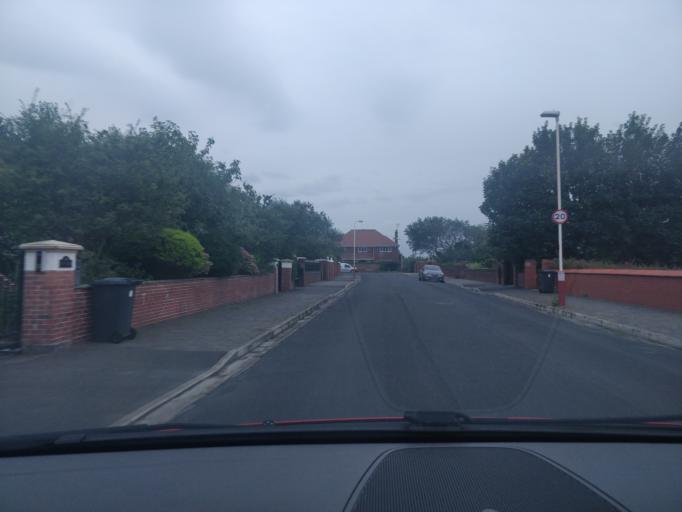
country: GB
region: England
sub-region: Sefton
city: Southport
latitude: 53.6321
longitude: -3.0356
